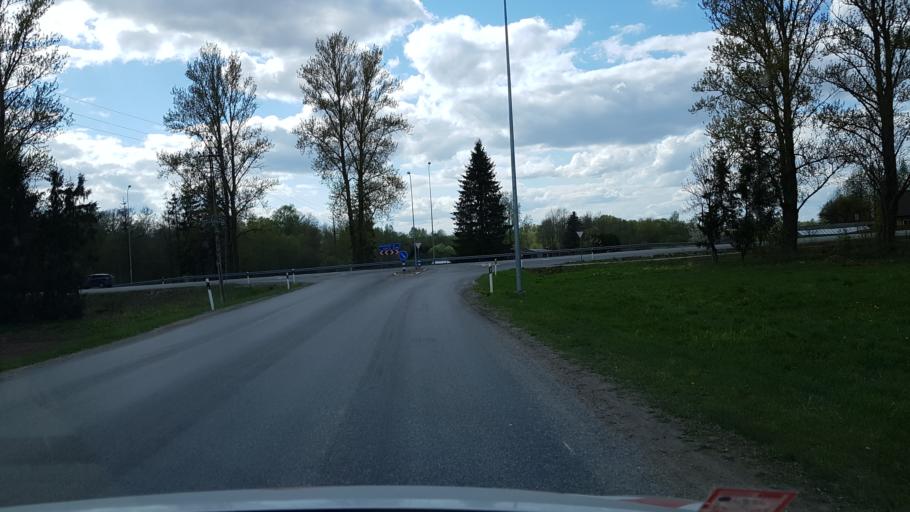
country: EE
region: Polvamaa
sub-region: Polva linn
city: Polva
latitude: 58.2824
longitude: 27.0035
